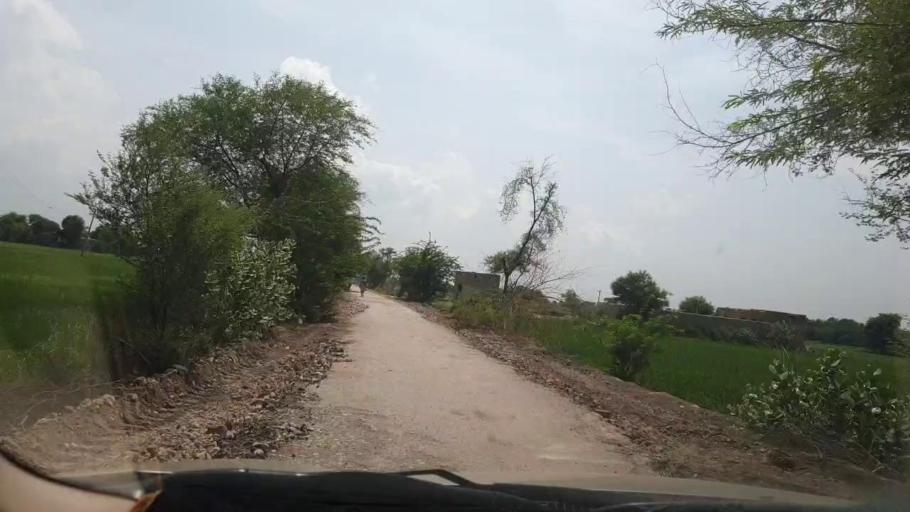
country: PK
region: Sindh
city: Larkana
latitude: 27.5762
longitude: 68.1136
